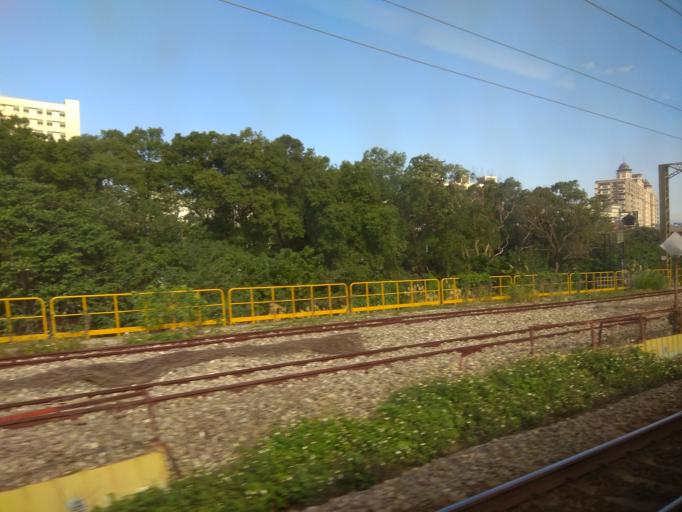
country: TW
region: Taiwan
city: Taoyuan City
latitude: 24.9761
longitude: 121.2690
